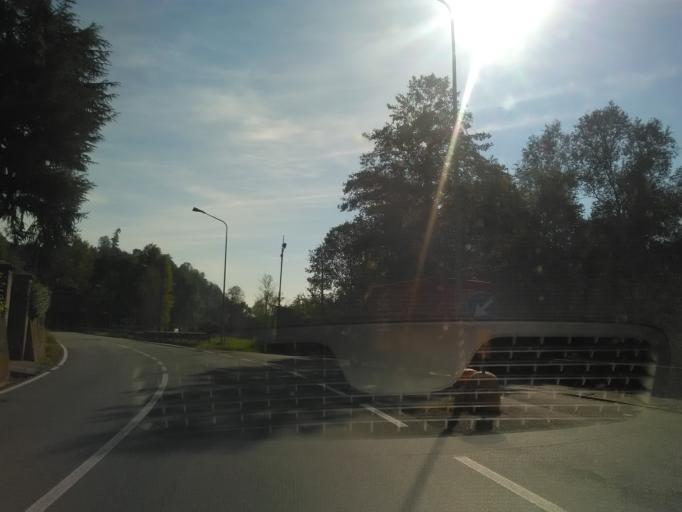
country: IT
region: Piedmont
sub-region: Provincia di Vercelli
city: Serravalle Sesia
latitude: 45.7028
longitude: 8.3014
